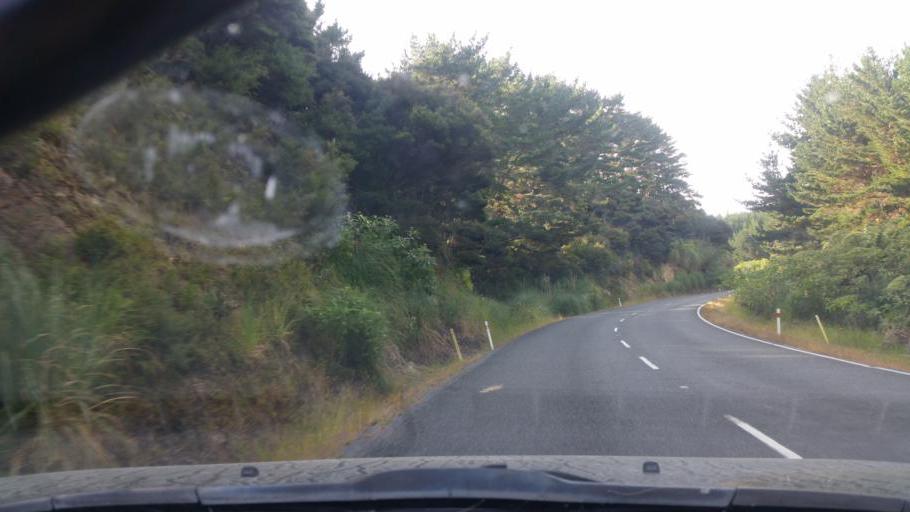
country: NZ
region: Northland
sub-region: Kaipara District
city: Dargaville
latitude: -36.2286
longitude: 174.0429
